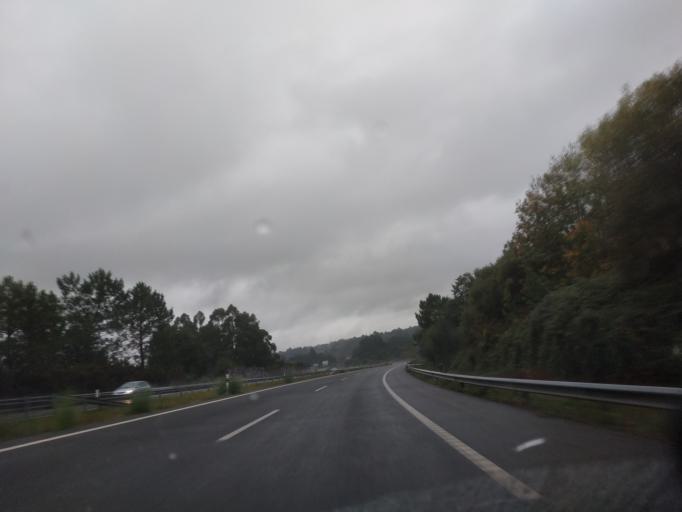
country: ES
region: Galicia
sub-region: Provincia da Coruna
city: Cambre
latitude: 43.2726
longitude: -8.3611
